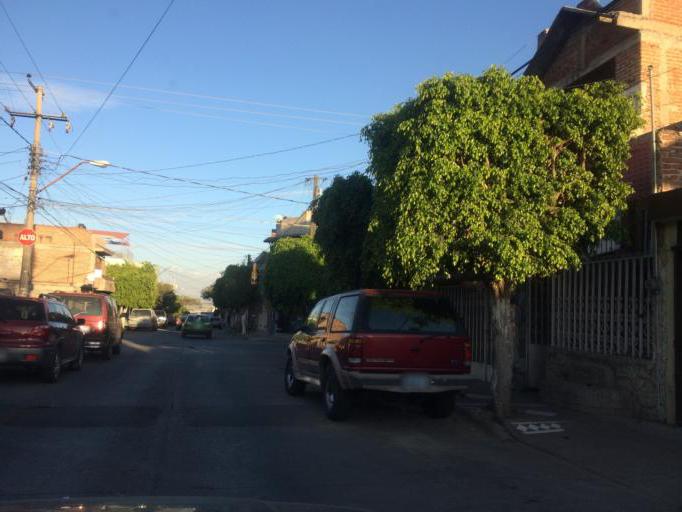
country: MX
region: Guanajuato
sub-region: Leon
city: La Ermita
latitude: 21.1367
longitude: -101.7089
